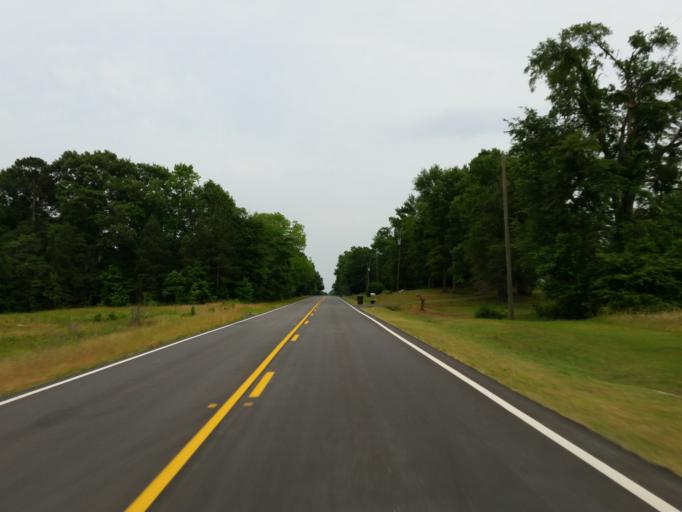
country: US
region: Georgia
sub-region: Dooly County
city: Unadilla
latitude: 32.3284
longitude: -83.7840
